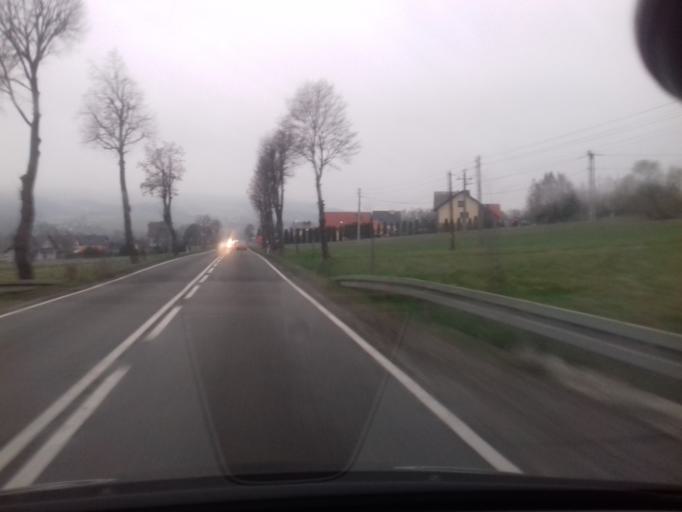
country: PL
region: Lesser Poland Voivodeship
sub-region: Powiat limanowski
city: Tymbark
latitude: 49.7221
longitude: 20.3543
